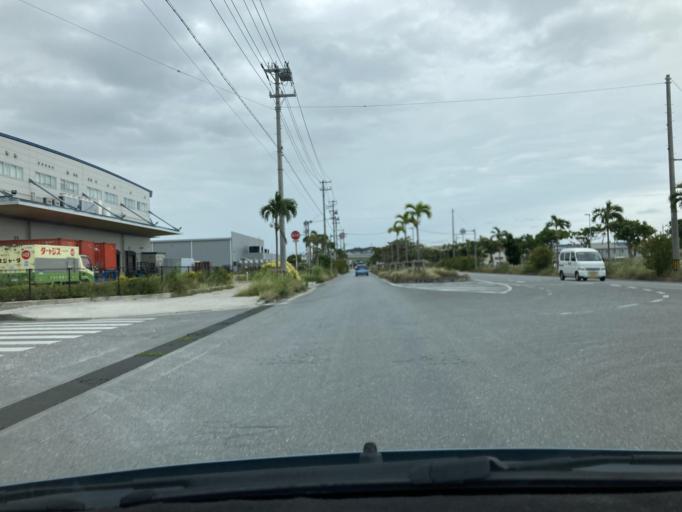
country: JP
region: Okinawa
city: Itoman
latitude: 26.1371
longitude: 127.6586
